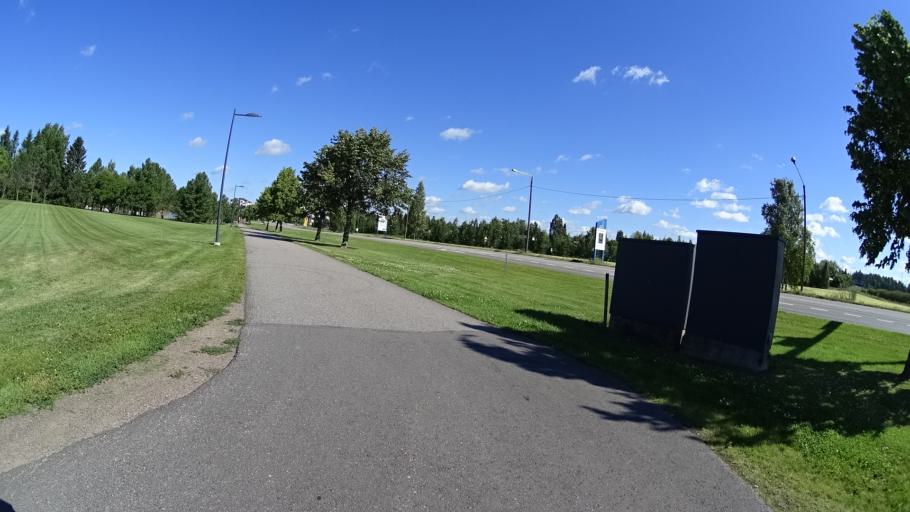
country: FI
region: Uusimaa
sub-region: Helsinki
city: Jaervenpaeae
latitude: 60.4629
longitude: 25.0861
